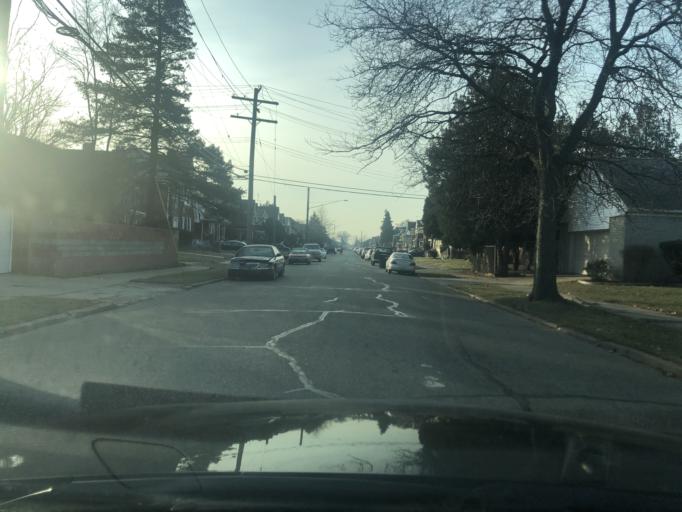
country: US
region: Michigan
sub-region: Wayne County
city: Highland Park
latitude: 42.3893
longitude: -83.1418
